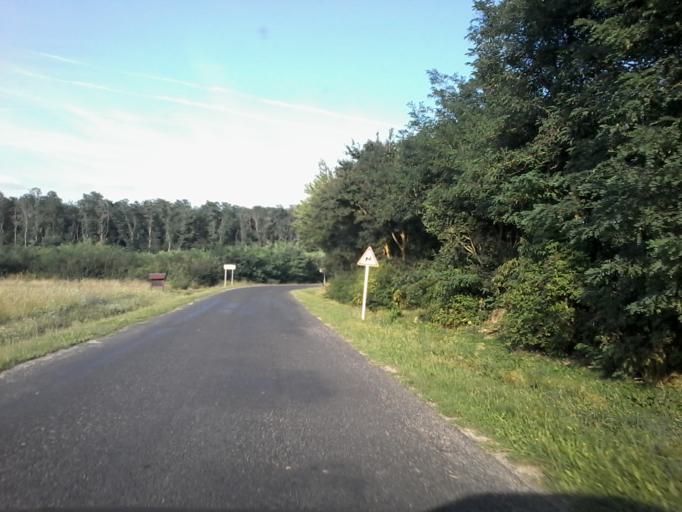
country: HU
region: Vas
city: Celldomolk
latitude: 47.2096
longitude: 17.0720
